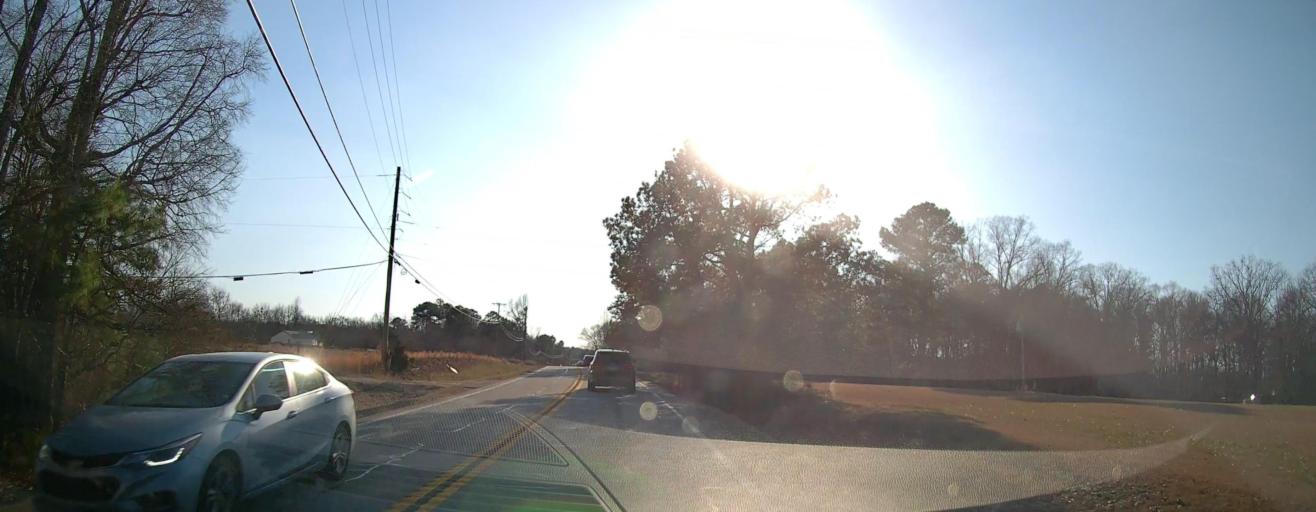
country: US
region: Georgia
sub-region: Henry County
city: Hampton
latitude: 33.4237
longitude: -84.2237
